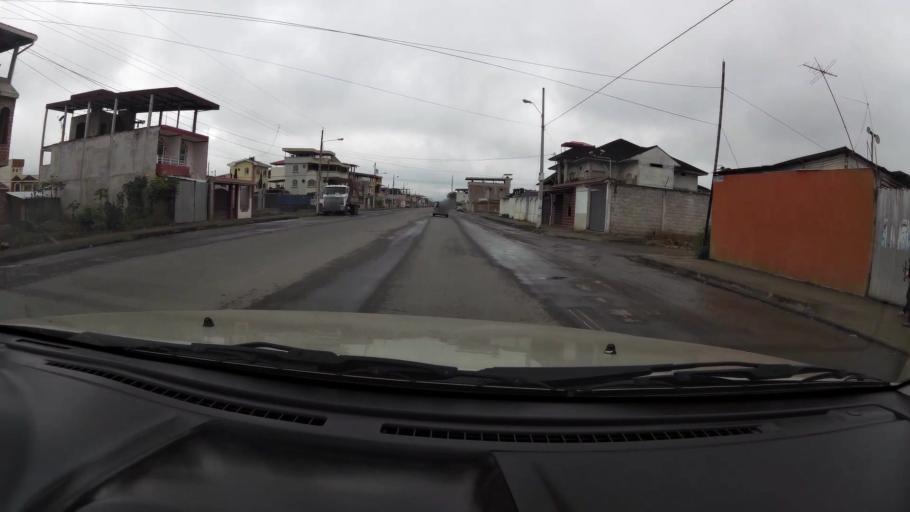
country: EC
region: El Oro
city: Pasaje
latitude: -3.3253
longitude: -79.8166
